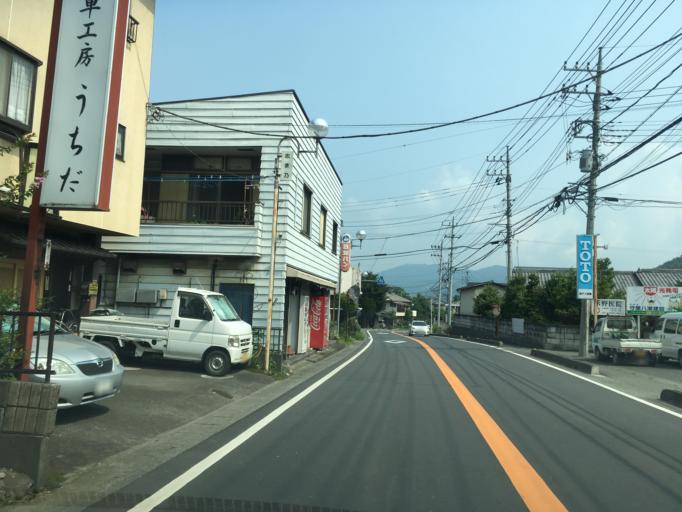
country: JP
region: Saitama
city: Chichibu
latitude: 36.0110
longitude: 139.1119
